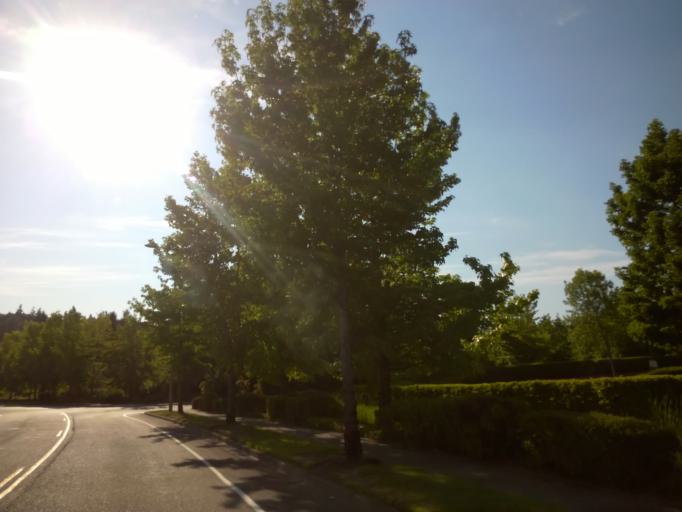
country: US
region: Washington
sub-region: King County
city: Bothell
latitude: 47.7788
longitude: -122.1860
